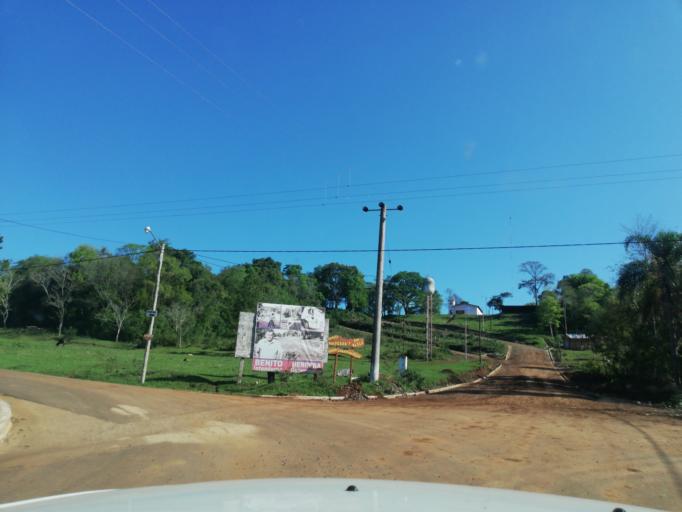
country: AR
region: Misiones
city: Arroyo del Medio
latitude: -27.6984
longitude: -55.4055
